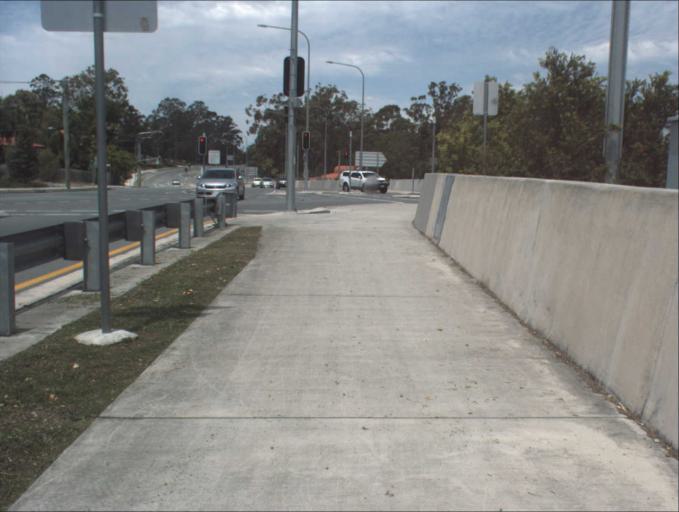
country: AU
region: Queensland
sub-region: Logan
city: Slacks Creek
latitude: -27.6432
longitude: 153.1456
